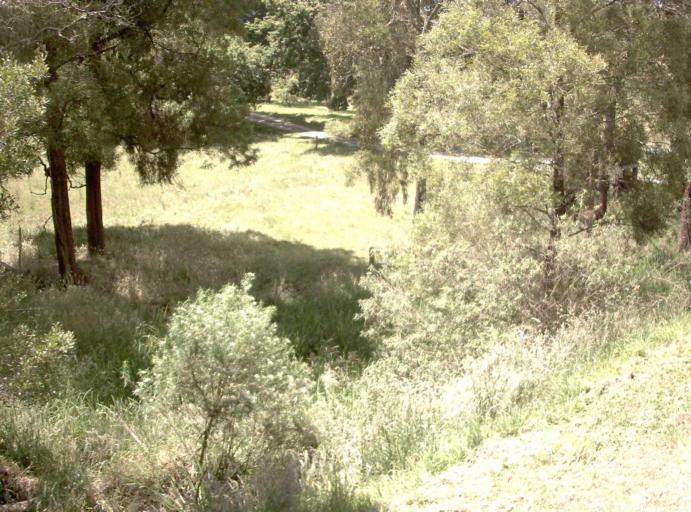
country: AU
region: Victoria
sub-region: Bass Coast
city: North Wonthaggi
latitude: -38.7202
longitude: 146.1202
